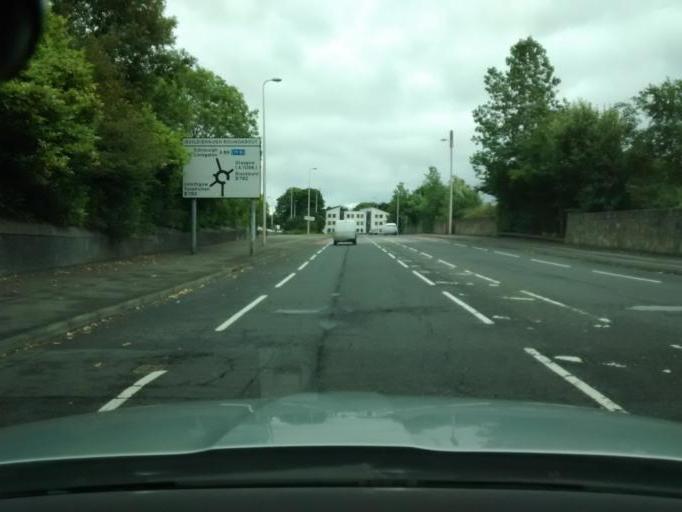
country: GB
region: Scotland
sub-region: West Lothian
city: Bathgate
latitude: 55.8949
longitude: -3.6264
